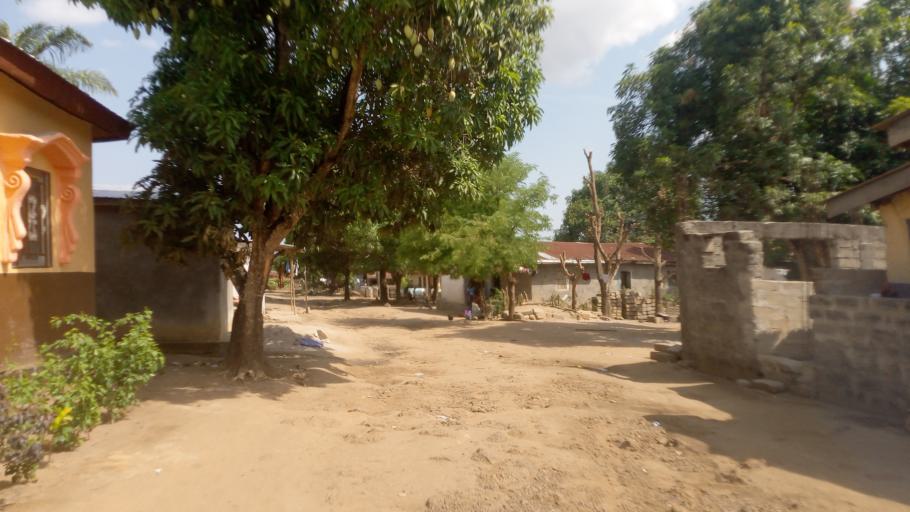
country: SL
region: Western Area
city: Waterloo
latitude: 8.3187
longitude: -13.0759
